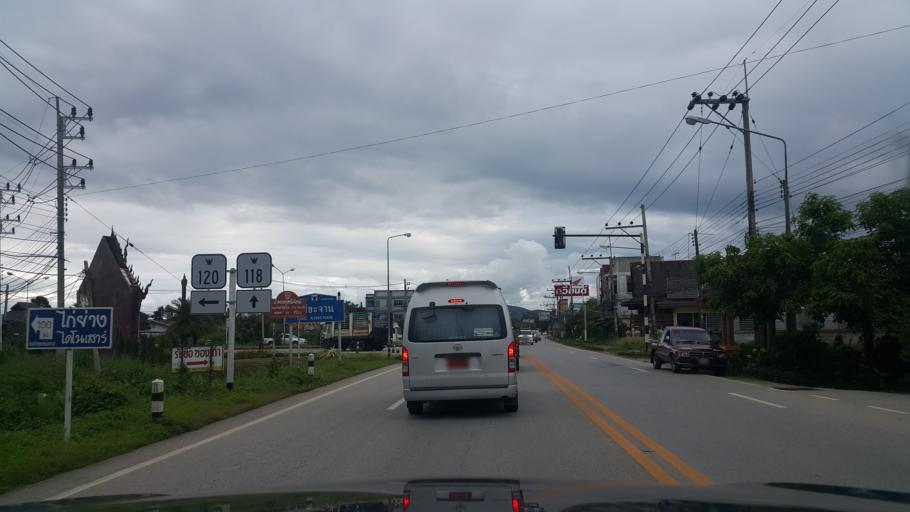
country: TH
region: Lampang
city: Wang Nuea
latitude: 19.2120
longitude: 99.5178
